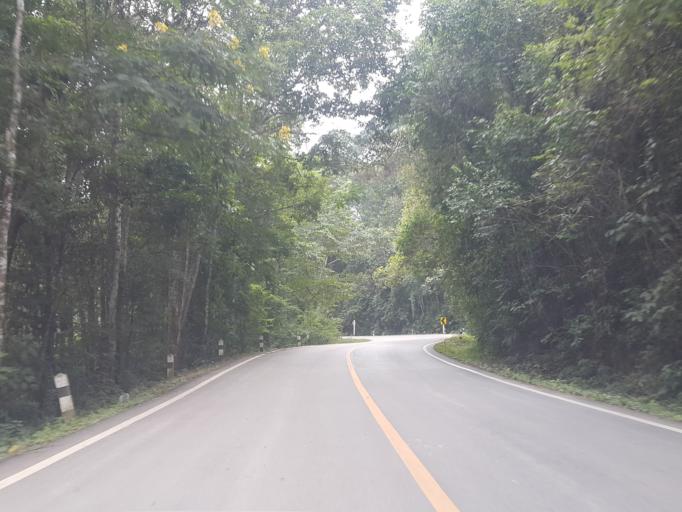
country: TH
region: Mae Hong Son
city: Mae Hi
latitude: 19.2403
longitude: 98.6577
